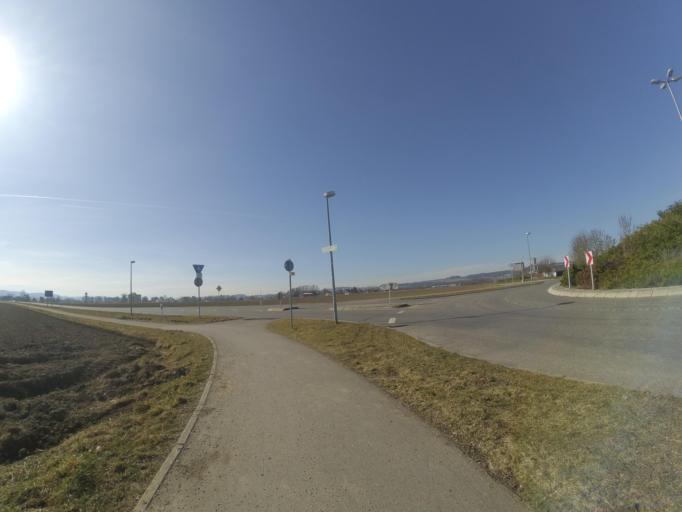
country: DE
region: Baden-Wuerttemberg
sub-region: Tuebingen Region
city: Baienfurt
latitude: 47.8357
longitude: 9.6378
